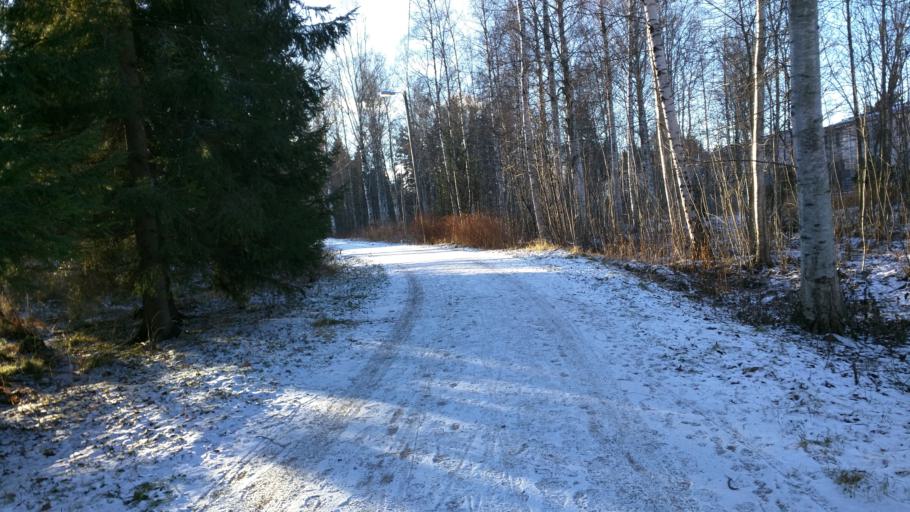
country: FI
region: Uusimaa
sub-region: Helsinki
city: Kilo
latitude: 60.2423
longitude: 24.7530
